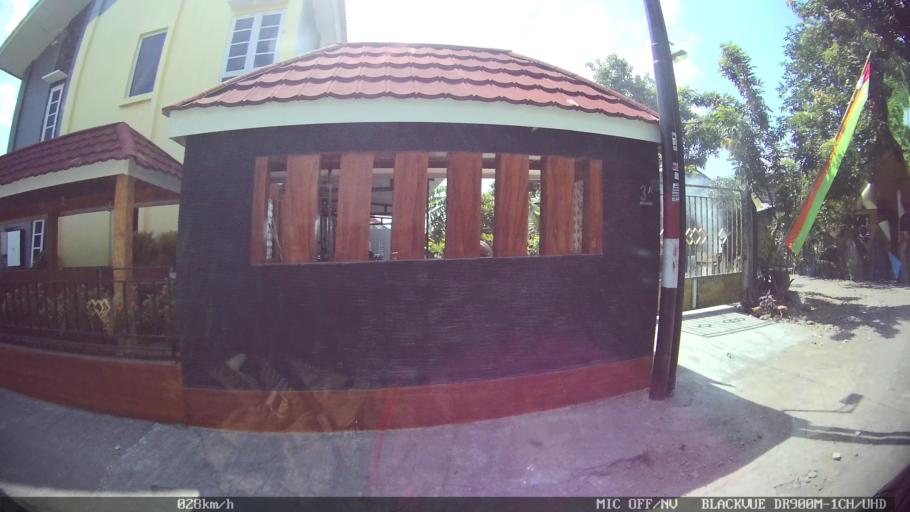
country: ID
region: Daerah Istimewa Yogyakarta
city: Sewon
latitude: -7.8351
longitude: 110.3792
